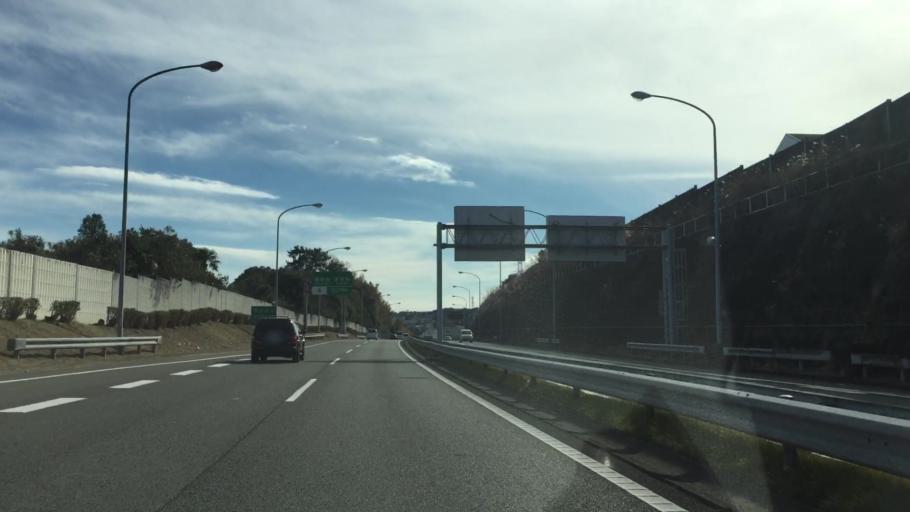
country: JP
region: Kanagawa
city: Kamakura
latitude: 35.3808
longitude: 139.5859
